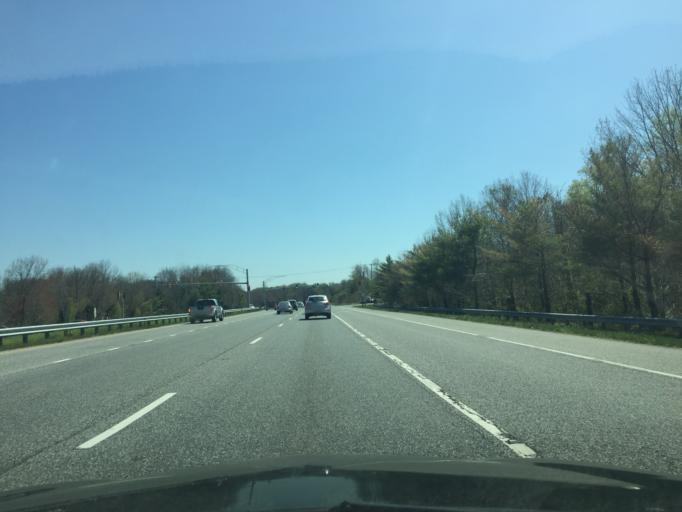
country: US
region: Maryland
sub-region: Harford County
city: South Bel Air
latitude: 39.5127
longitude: -76.3422
